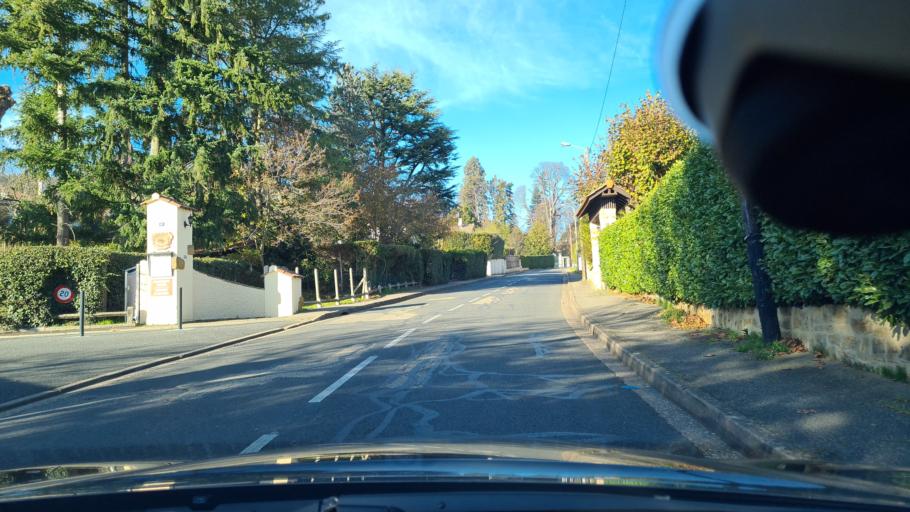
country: FR
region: Rhone-Alpes
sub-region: Departement du Rhone
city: Fontaines-sur-Saone
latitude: 45.8213
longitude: 4.8107
